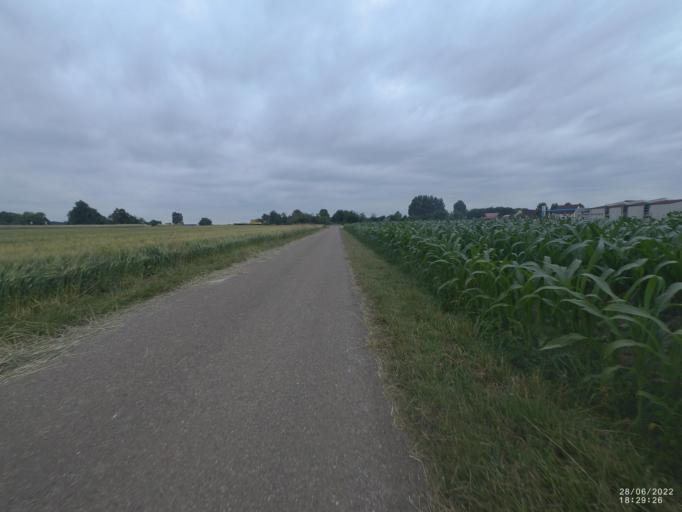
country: DE
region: Baden-Wuerttemberg
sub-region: Regierungsbezirk Stuttgart
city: Gerstetten
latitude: 48.6166
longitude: 10.0265
